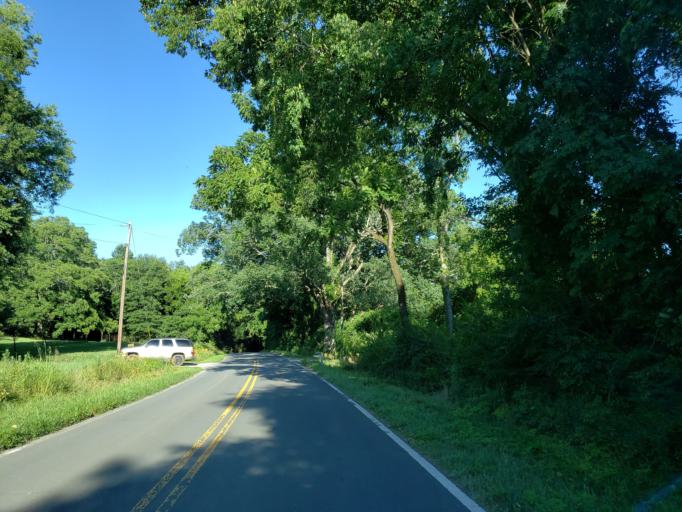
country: US
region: Georgia
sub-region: Polk County
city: Aragon
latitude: 34.0992
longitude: -85.0032
